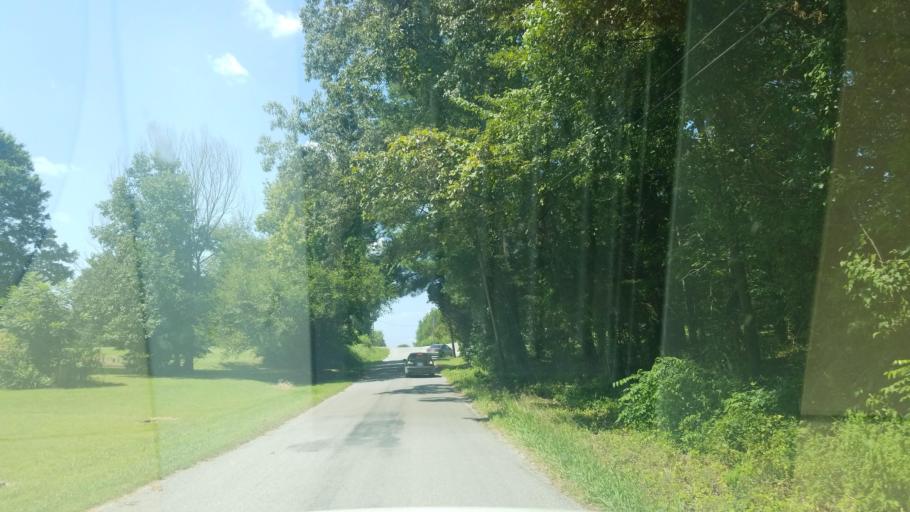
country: US
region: Illinois
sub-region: Saline County
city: Carrier Mills
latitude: 37.7941
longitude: -88.6462
